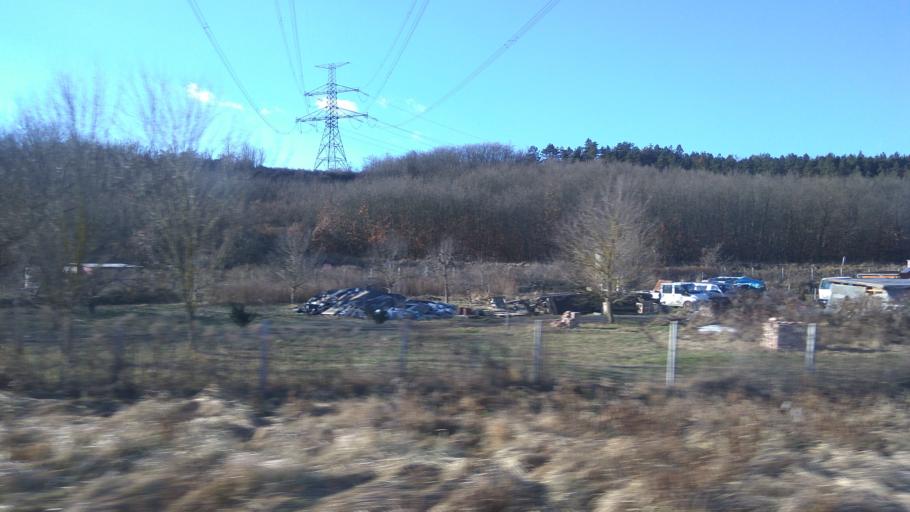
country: HU
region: Pest
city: Pecel
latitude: 47.5008
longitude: 19.3719
